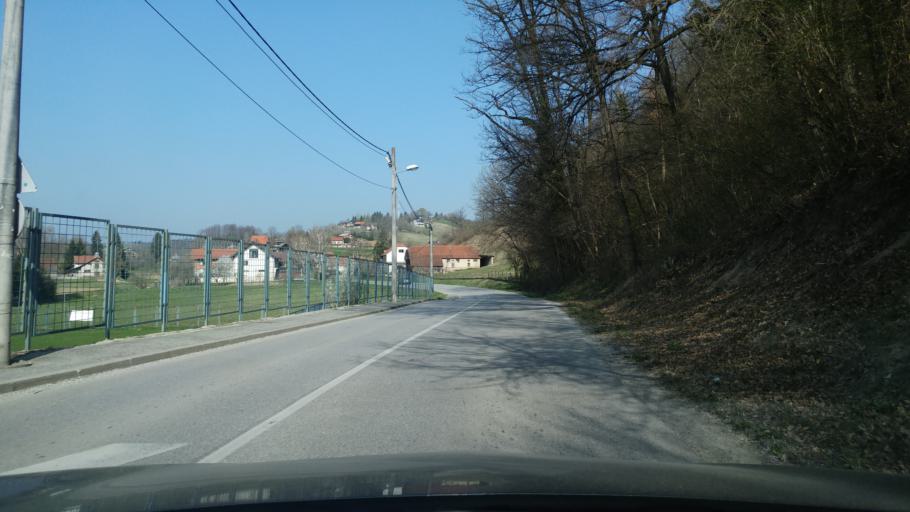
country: HR
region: Zagrebacka
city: Pojatno
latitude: 45.9171
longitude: 15.7753
